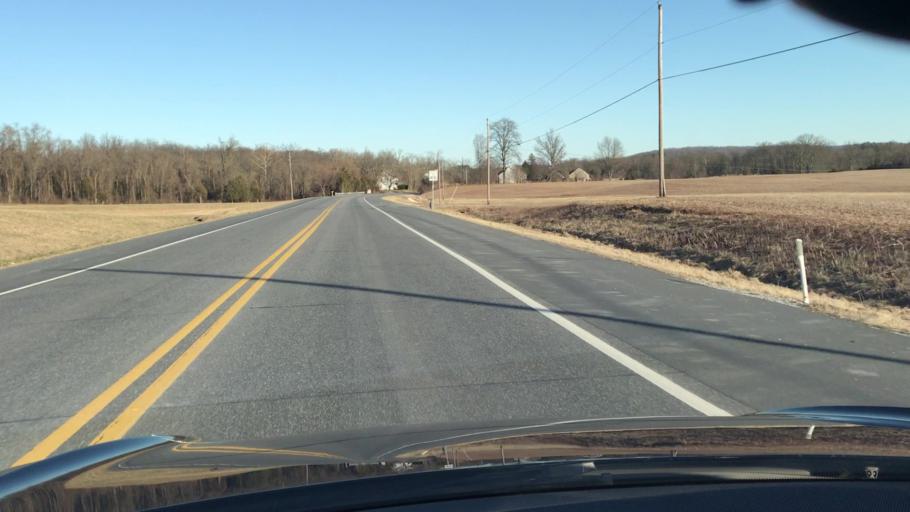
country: US
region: Pennsylvania
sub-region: Cumberland County
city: Lower Allen
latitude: 40.1463
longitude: -76.8797
